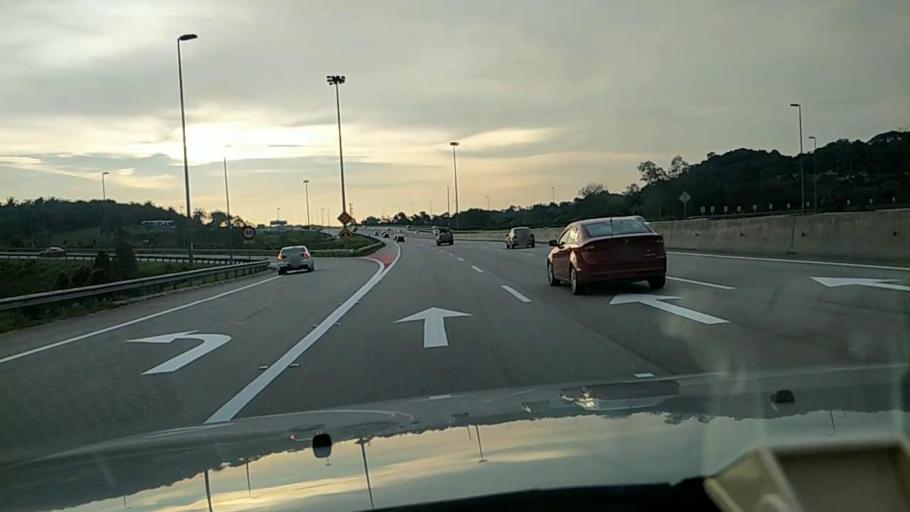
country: MY
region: Selangor
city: Kuang
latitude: 3.2695
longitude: 101.5451
